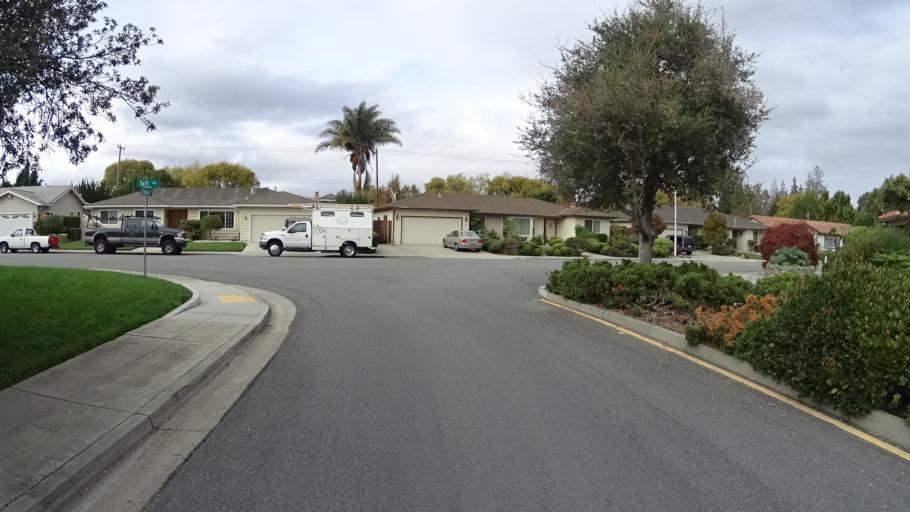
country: US
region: California
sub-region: Santa Clara County
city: Santa Clara
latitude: 37.3334
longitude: -121.9694
